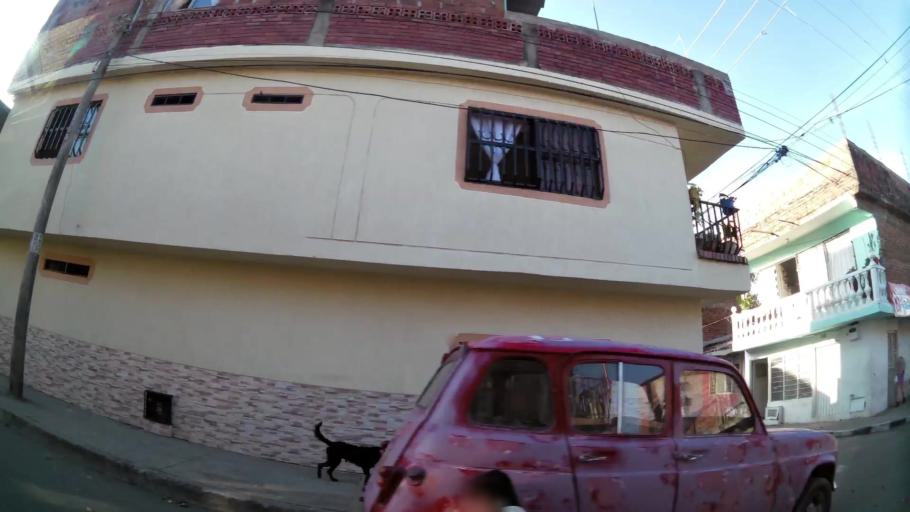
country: CO
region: Valle del Cauca
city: Cali
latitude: 3.4094
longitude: -76.5001
